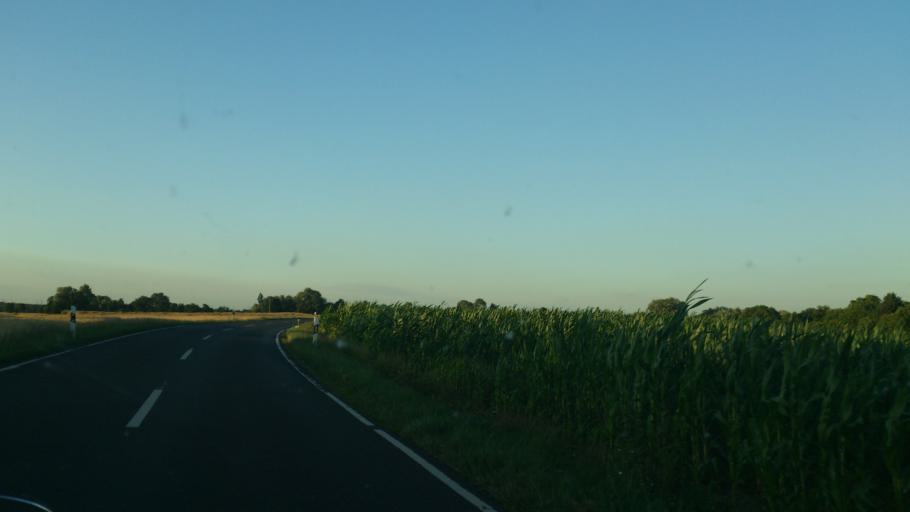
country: DE
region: Hesse
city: Raunheim
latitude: 50.0193
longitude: 8.4431
